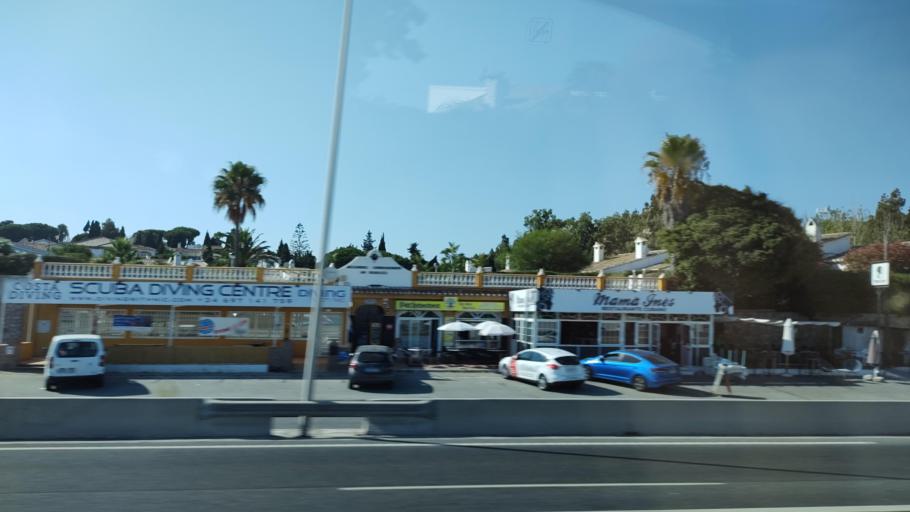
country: ES
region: Andalusia
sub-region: Provincia de Malaga
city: Fuengirola
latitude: 36.5065
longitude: -4.6651
